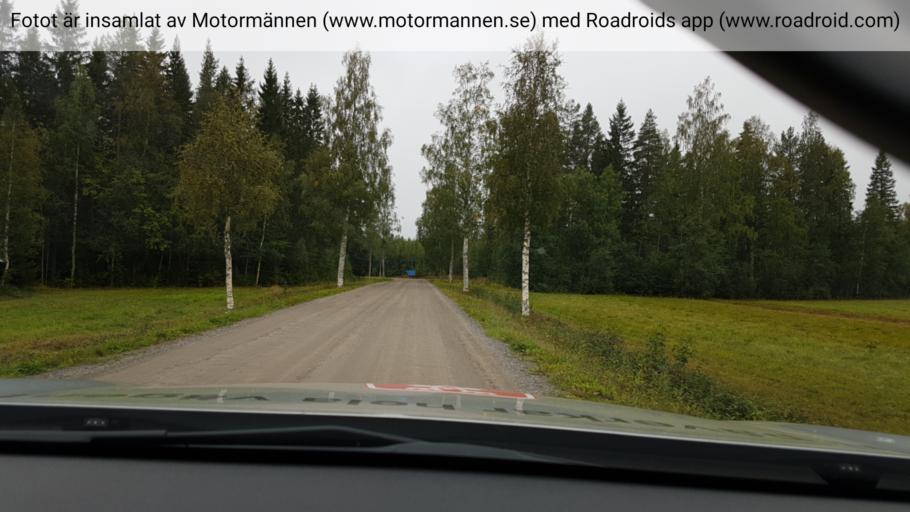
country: SE
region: Vaesterbotten
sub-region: Skelleftea Kommun
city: Burtraesk
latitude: 64.4652
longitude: 20.4668
